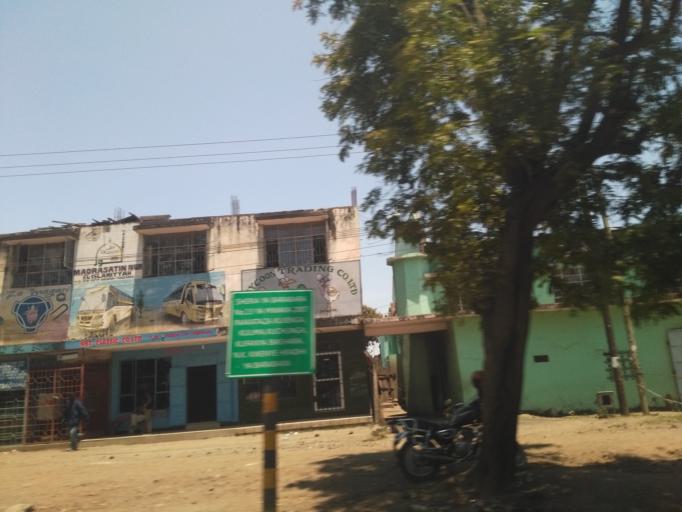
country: TZ
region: Arusha
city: Arusha
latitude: -3.3748
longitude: 36.6744
